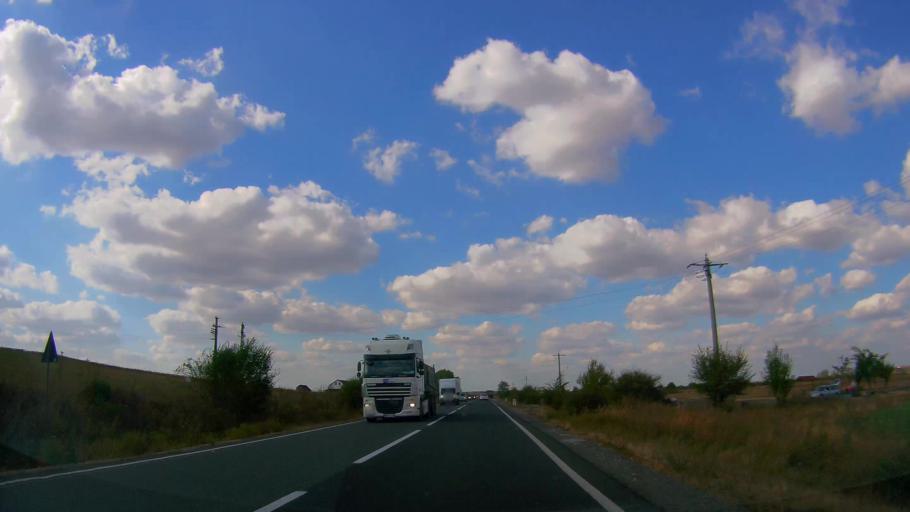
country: RO
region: Satu Mare
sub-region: Oras Ardud
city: Ardud
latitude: 47.6100
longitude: 22.8800
